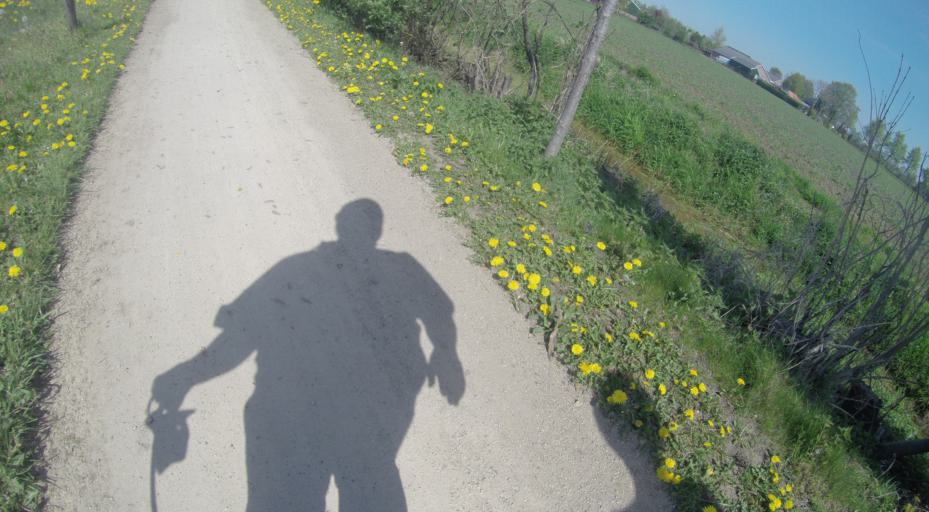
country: NL
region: Gelderland
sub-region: Oost Gelre
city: Lichtenvoorde
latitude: 51.9962
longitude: 6.5224
